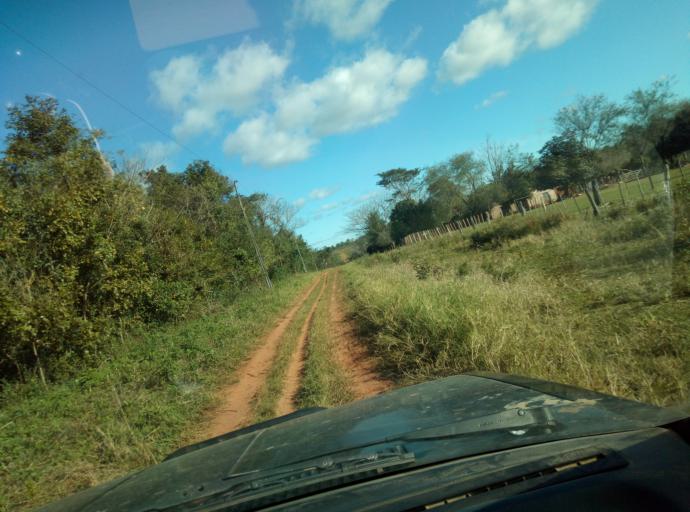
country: PY
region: Caaguazu
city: Doctor Cecilio Baez
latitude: -25.1691
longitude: -56.2729
